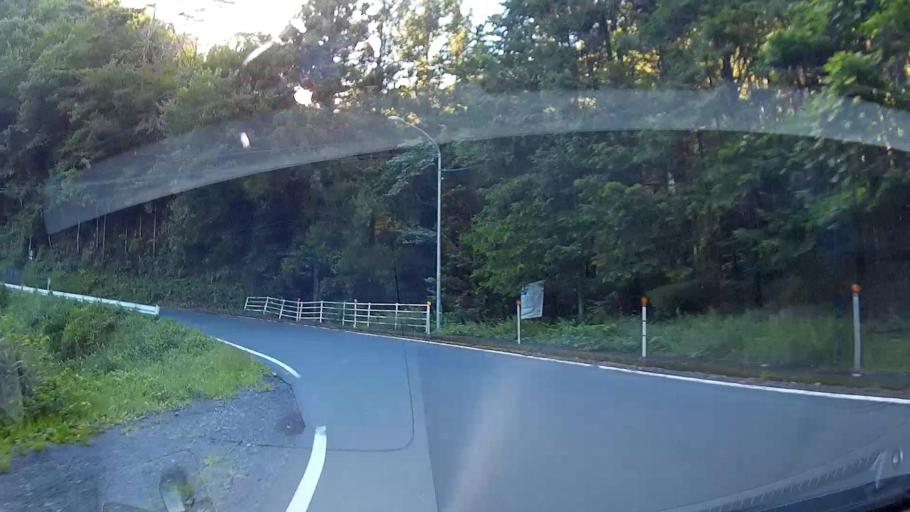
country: JP
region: Shizuoka
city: Shizuoka-shi
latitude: 35.2206
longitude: 138.2311
